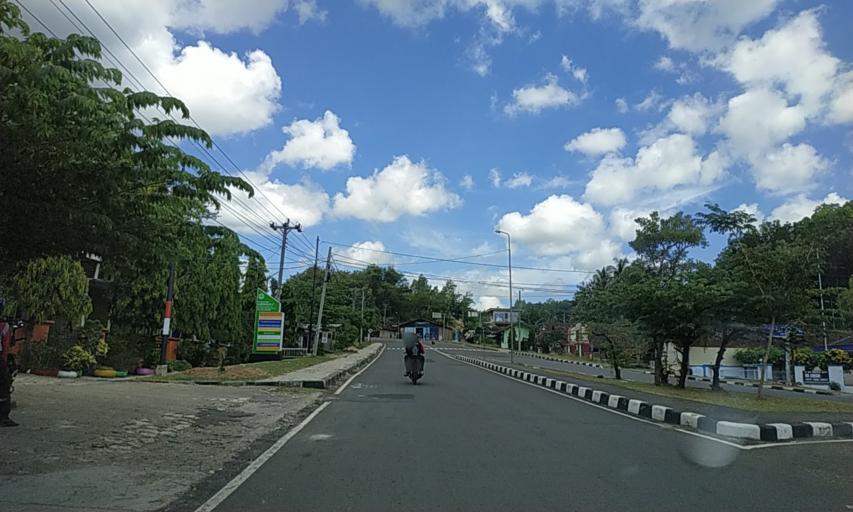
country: ID
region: East Java
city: Krajan
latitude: -8.0300
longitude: 110.9388
